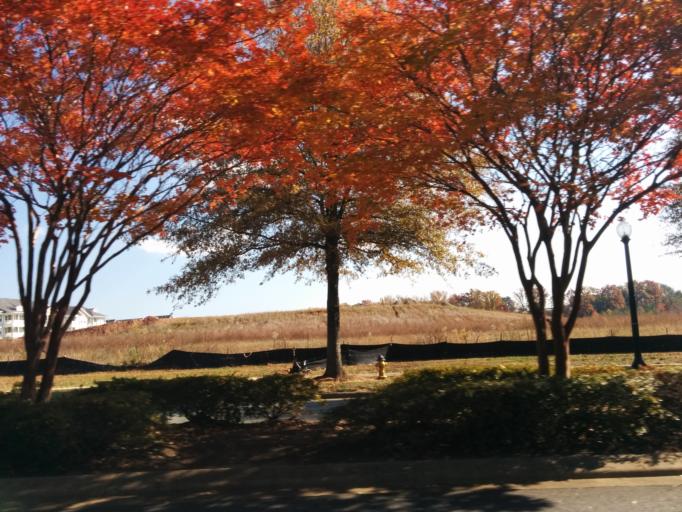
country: US
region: North Carolina
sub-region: Iredell County
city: Mooresville
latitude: 35.5876
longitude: -80.8817
